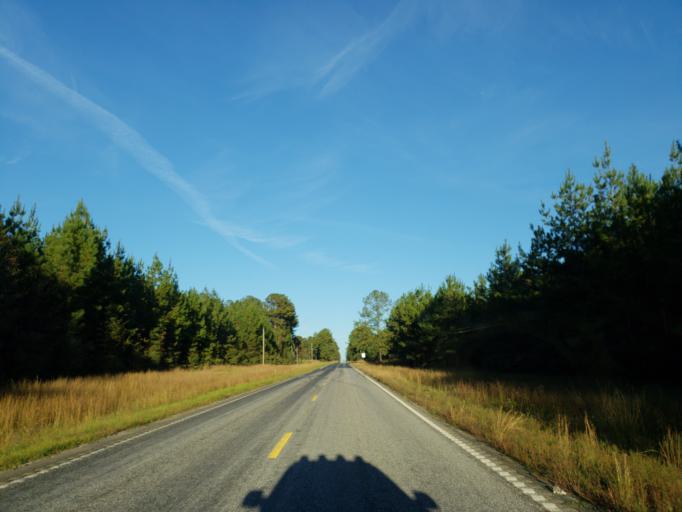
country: US
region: Mississippi
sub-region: Wayne County
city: Belmont
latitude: 31.4118
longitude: -88.6024
